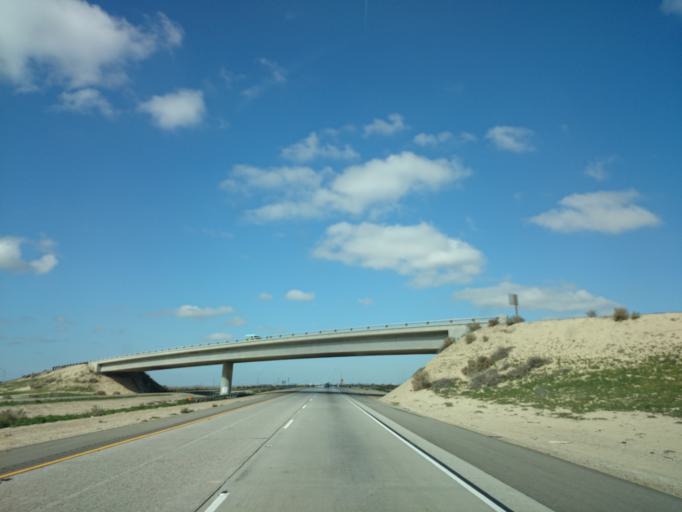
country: US
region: California
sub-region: Kern County
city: Buttonwillow
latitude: 35.3544
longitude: -119.3349
